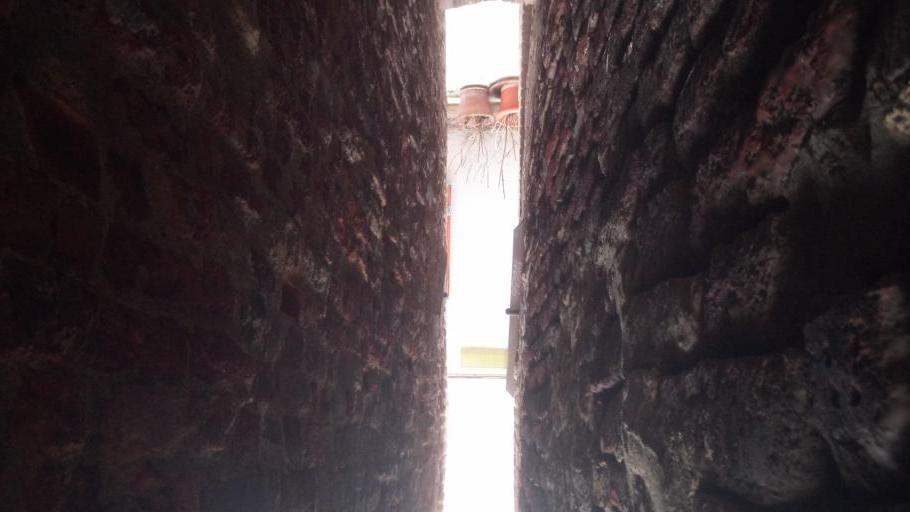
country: IT
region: The Marches
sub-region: Provincia di Ascoli Piceno
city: Ripatransone
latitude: 42.9990
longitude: 13.7626
